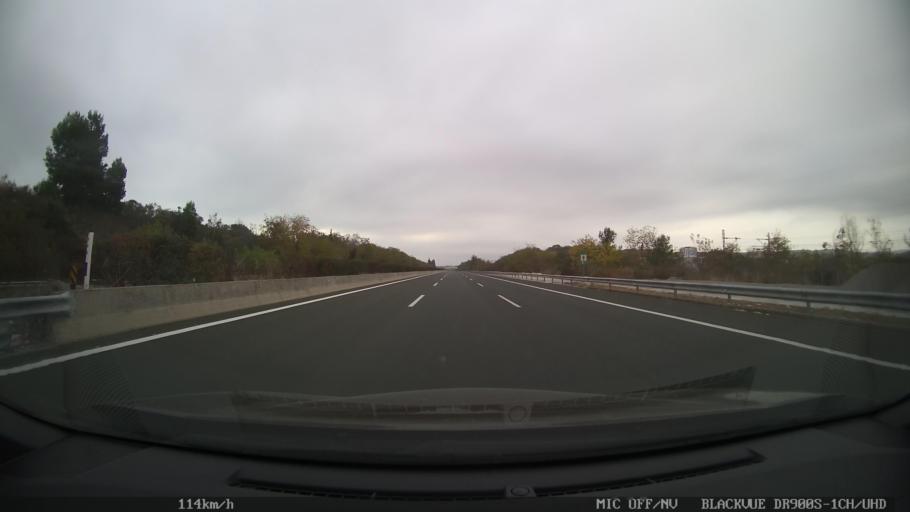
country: GR
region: Central Macedonia
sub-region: Nomos Pierias
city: Aiginio
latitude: 40.4828
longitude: 22.5676
